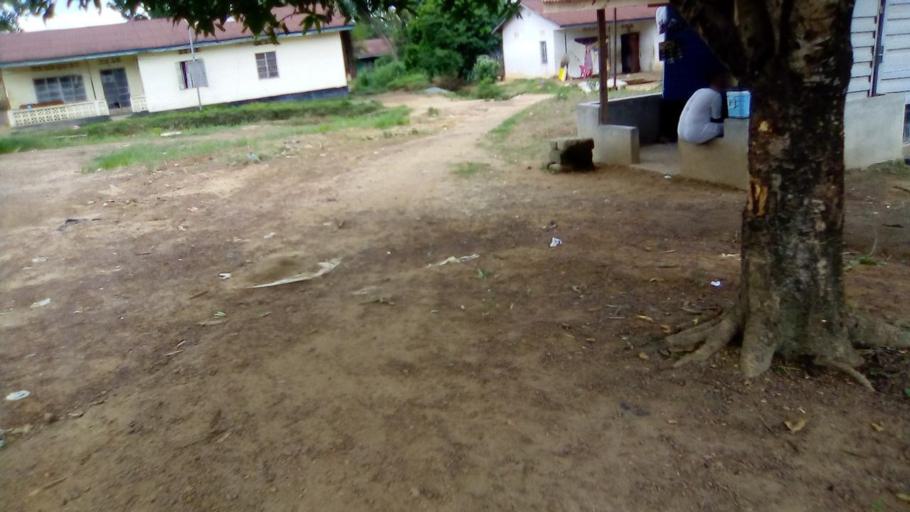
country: SL
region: Southern Province
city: Bo
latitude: 7.9588
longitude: -11.7218
